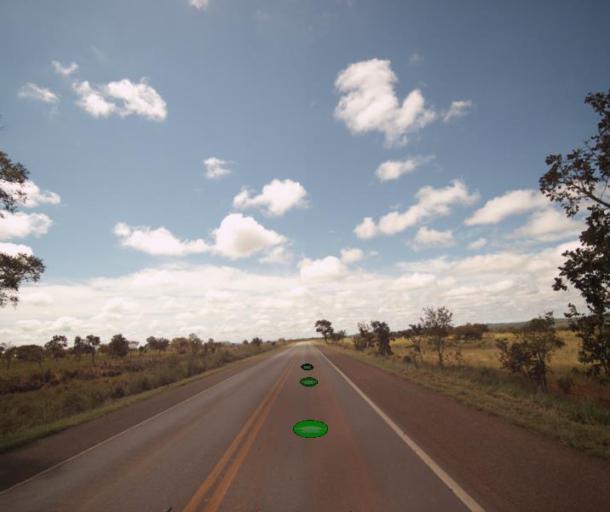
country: BR
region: Goias
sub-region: Padre Bernardo
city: Padre Bernardo
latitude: -15.1501
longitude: -48.3427
